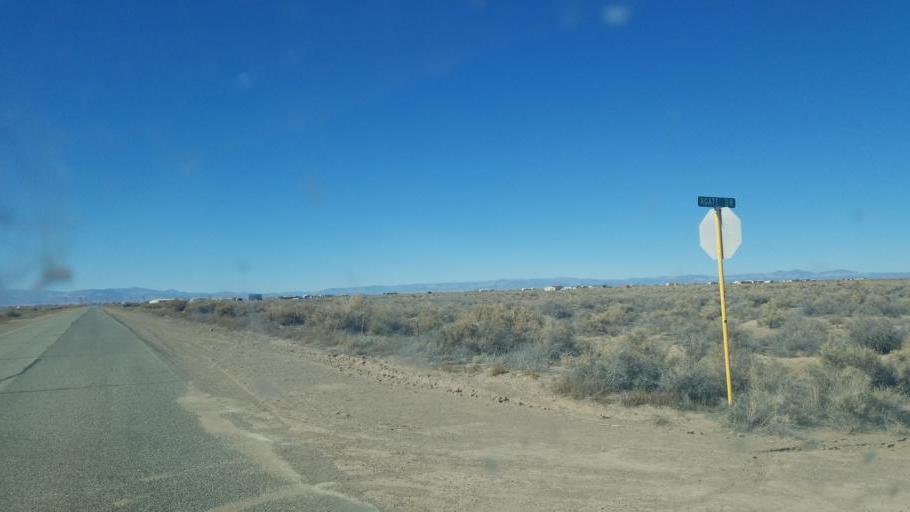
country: US
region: Colorado
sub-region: Alamosa County
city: Alamosa
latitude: 37.5748
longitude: -105.8936
